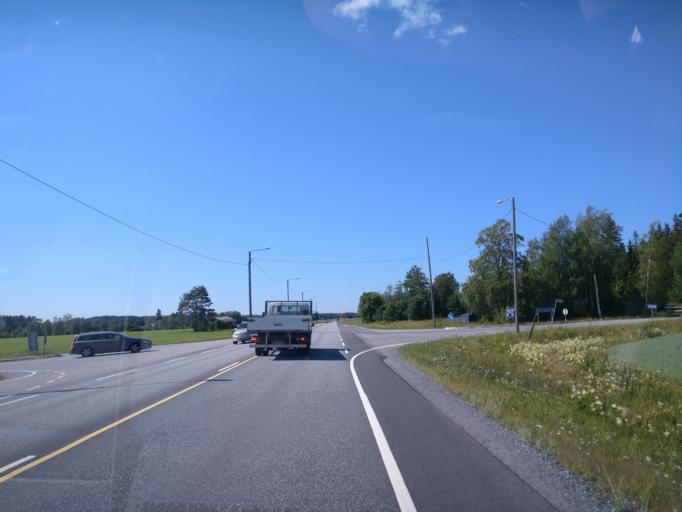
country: FI
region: Satakunta
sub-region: Pori
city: Nakkila
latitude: 61.4597
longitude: 22.0123
